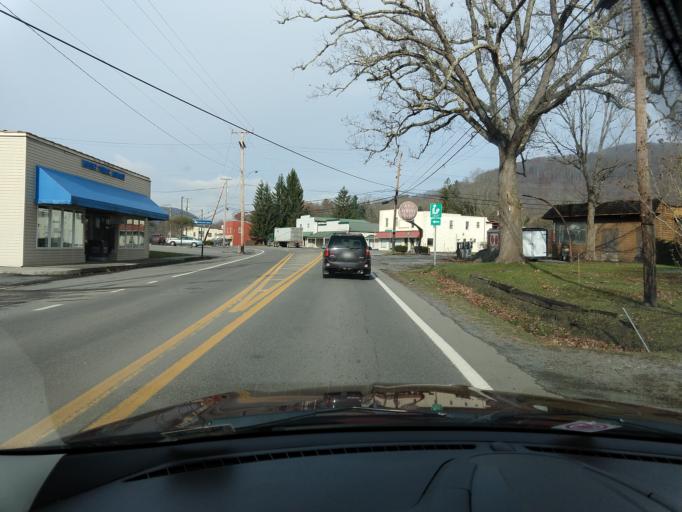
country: US
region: West Virginia
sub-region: Greenbrier County
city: Rainelle
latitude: 37.9625
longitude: -80.6876
